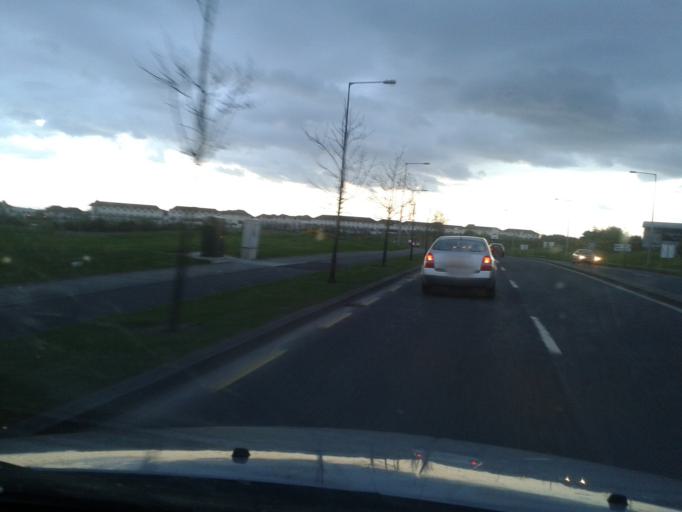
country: IE
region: Leinster
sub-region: Fingal County
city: Swords
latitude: 53.4465
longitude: -6.2191
